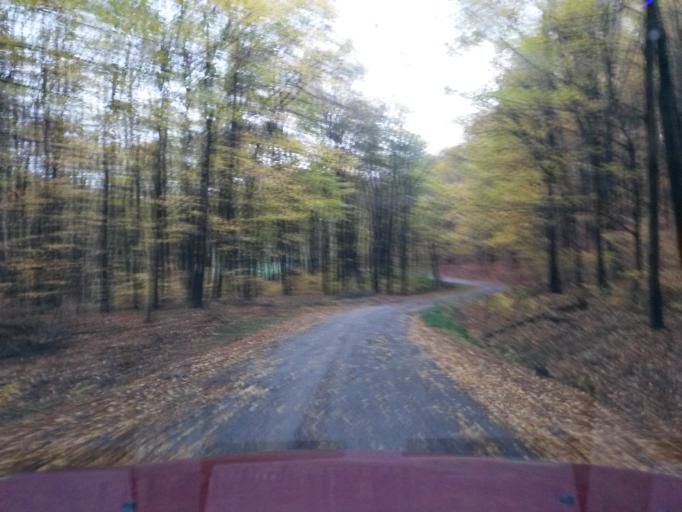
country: SK
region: Kosicky
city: Kosice
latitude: 48.7829
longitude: 21.2364
